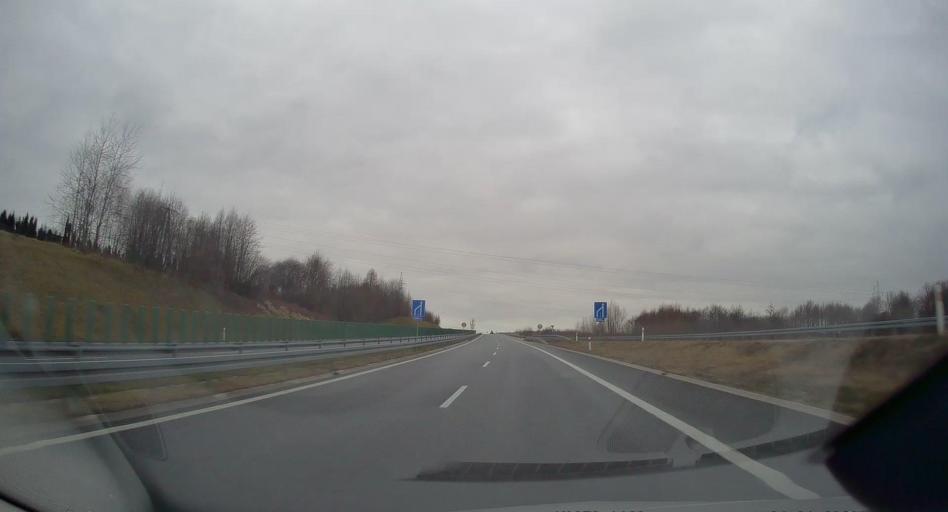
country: PL
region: Subcarpathian Voivodeship
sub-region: Powiat ropczycko-sedziszowski
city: Ropczyce
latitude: 50.0572
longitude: 21.5949
